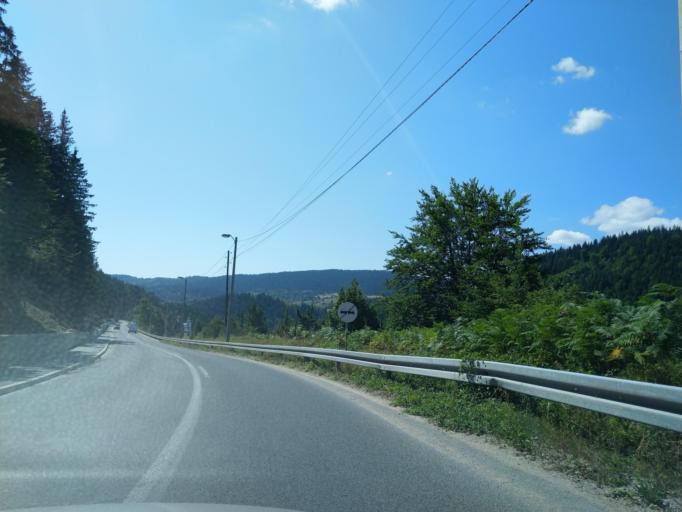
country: RS
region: Central Serbia
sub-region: Zlatiborski Okrug
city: Nova Varos
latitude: 43.4423
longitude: 19.8200
